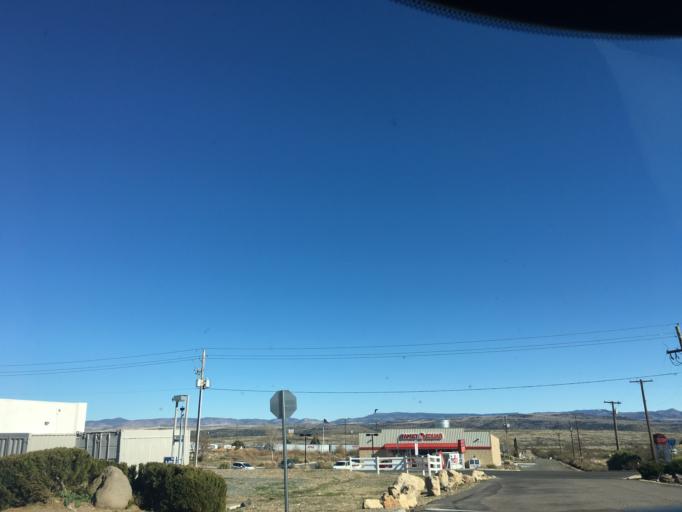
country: US
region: Arizona
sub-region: Yavapai County
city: Cordes Lakes
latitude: 34.3259
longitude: -112.1194
